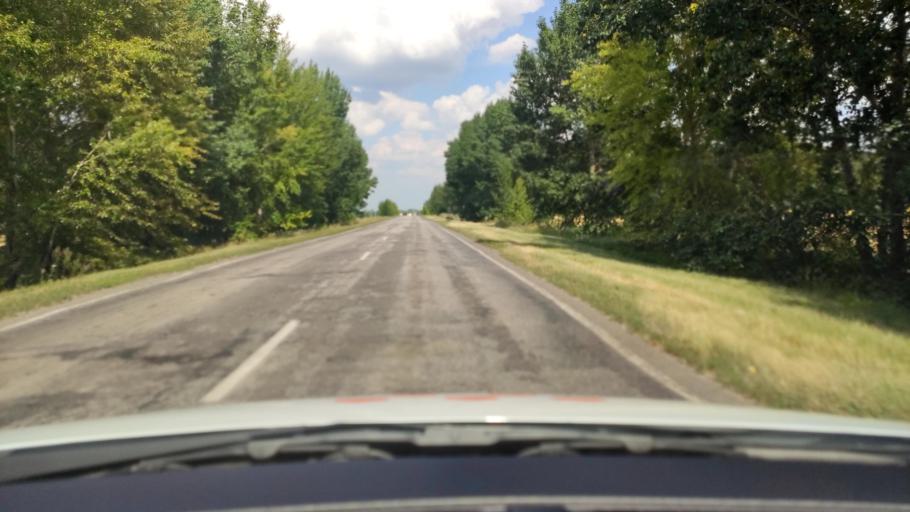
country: RU
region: Voronezj
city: Pereleshinskiy
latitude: 51.7347
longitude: 40.3867
